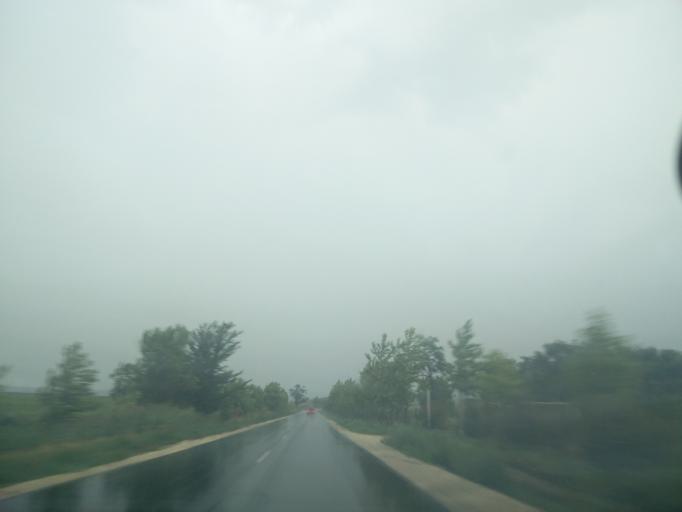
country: HU
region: Fejer
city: Etyek
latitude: 47.4521
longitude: 18.7674
